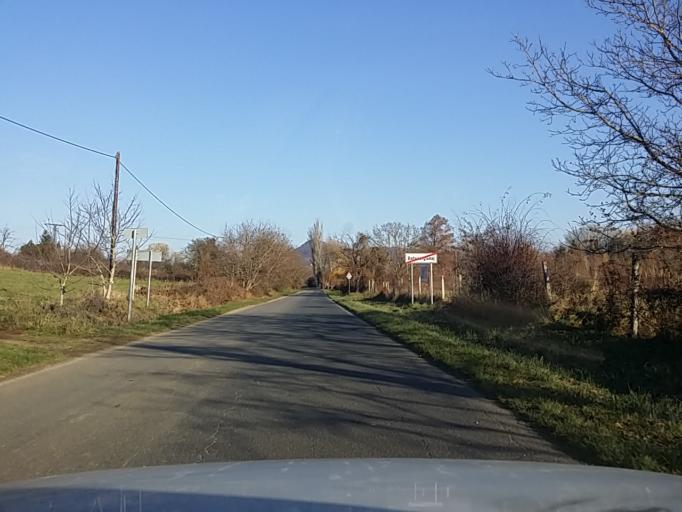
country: HU
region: Veszprem
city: Badacsonytomaj
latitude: 46.8114
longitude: 17.5149
